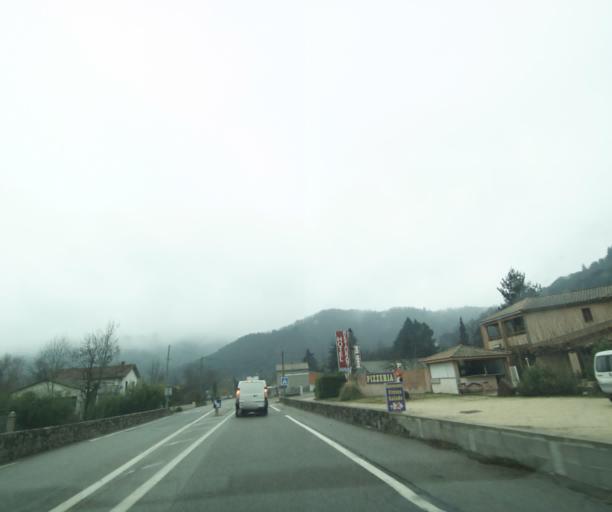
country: FR
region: Rhone-Alpes
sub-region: Departement de l'Ardeche
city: Jaujac
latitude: 44.6626
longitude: 4.2964
